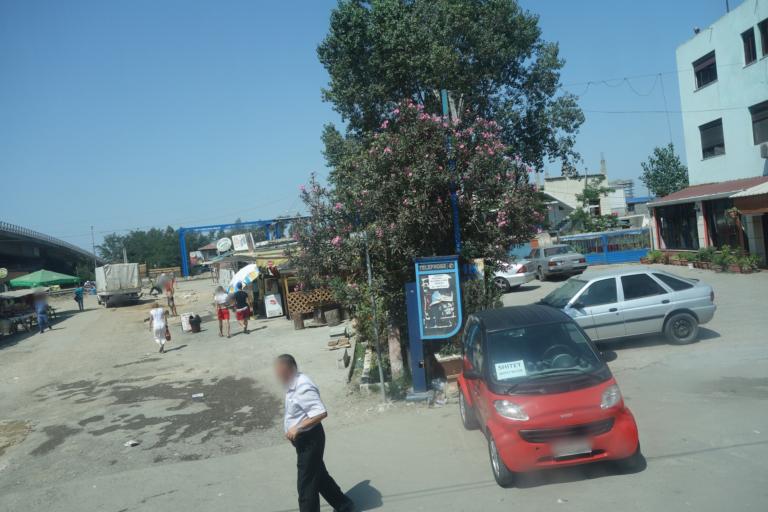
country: AL
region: Durres
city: Durres
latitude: 41.3163
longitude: 19.4706
